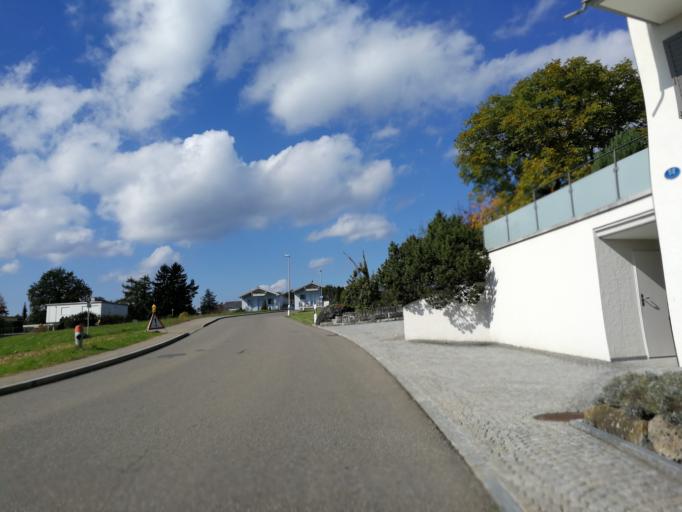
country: CH
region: Zurich
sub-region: Bezirk Meilen
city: Obermeilen
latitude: 47.2719
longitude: 8.6681
